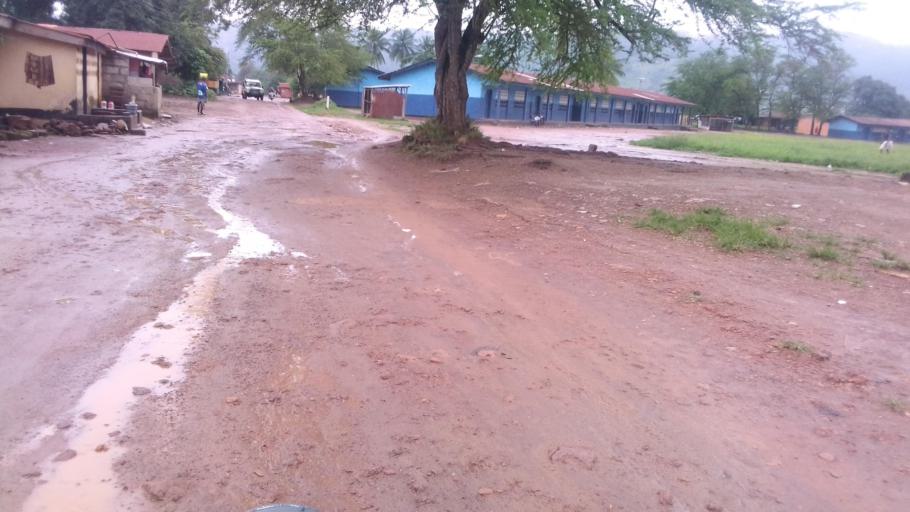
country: SL
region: Eastern Province
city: Kenema
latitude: 7.8869
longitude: -11.1819
